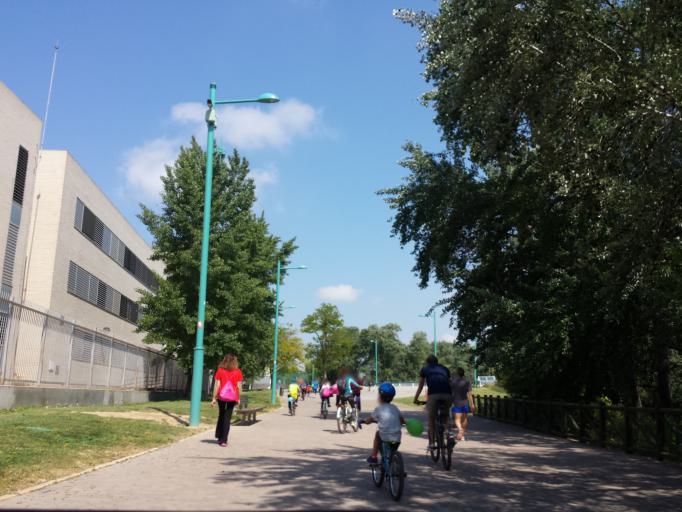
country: ES
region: Aragon
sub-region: Provincia de Zaragoza
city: Almozara
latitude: 41.6631
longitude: -0.8950
